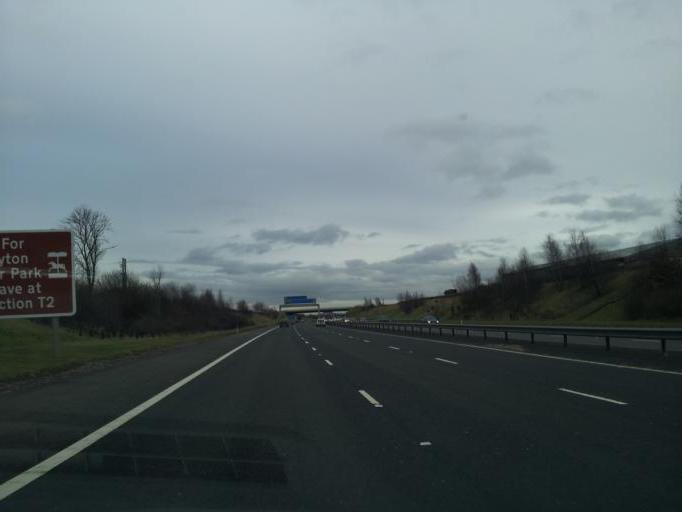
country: GB
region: England
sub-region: Staffordshire
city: Shenstone
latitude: 52.6469
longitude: -1.8315
